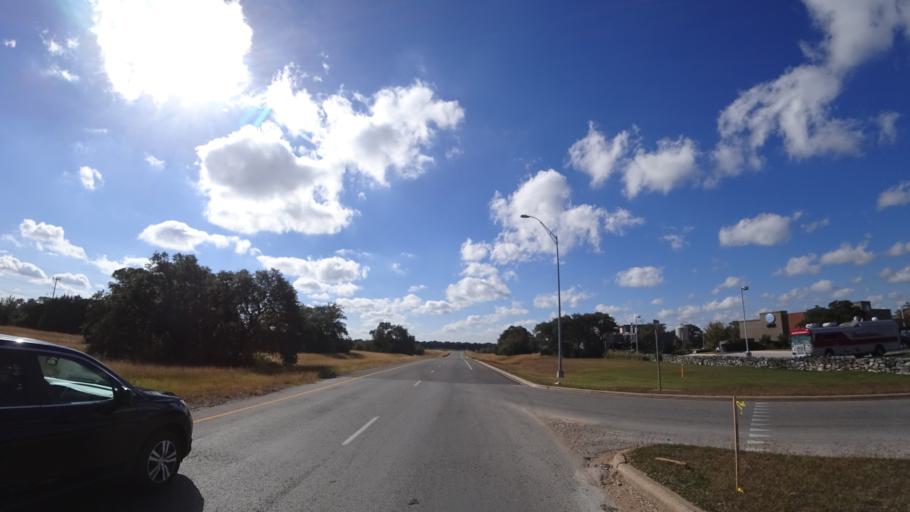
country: US
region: Texas
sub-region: Travis County
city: Shady Hollow
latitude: 30.2009
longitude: -97.8669
